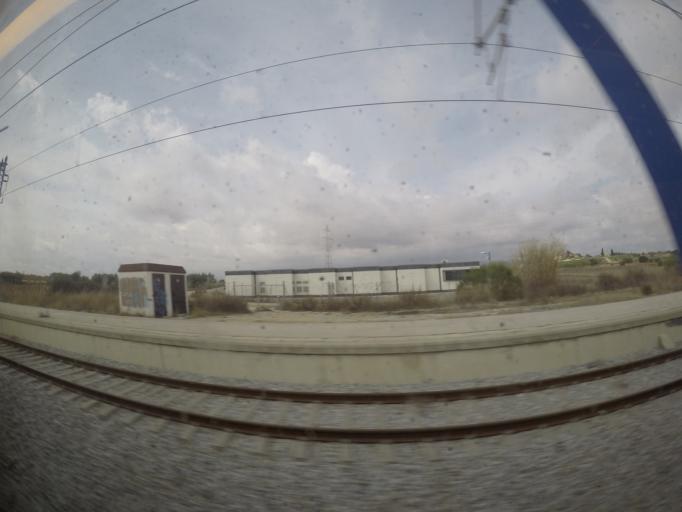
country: ES
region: Catalonia
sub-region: Provincia de Tarragona
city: Santa Oliva
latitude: 41.2508
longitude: 1.5730
